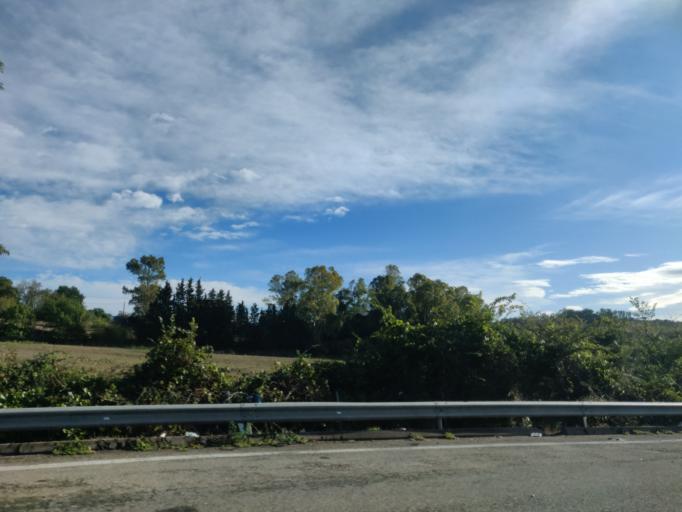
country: IT
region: Tuscany
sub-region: Provincia di Grosseto
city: Ribolla
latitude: 42.9191
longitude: 11.0067
